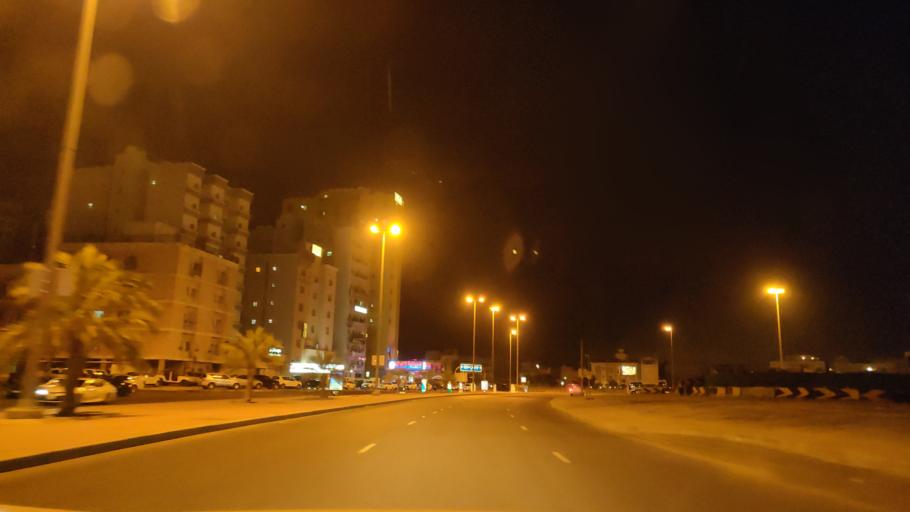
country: KW
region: Muhafazat Hawalli
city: As Salimiyah
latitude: 29.3265
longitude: 48.0847
